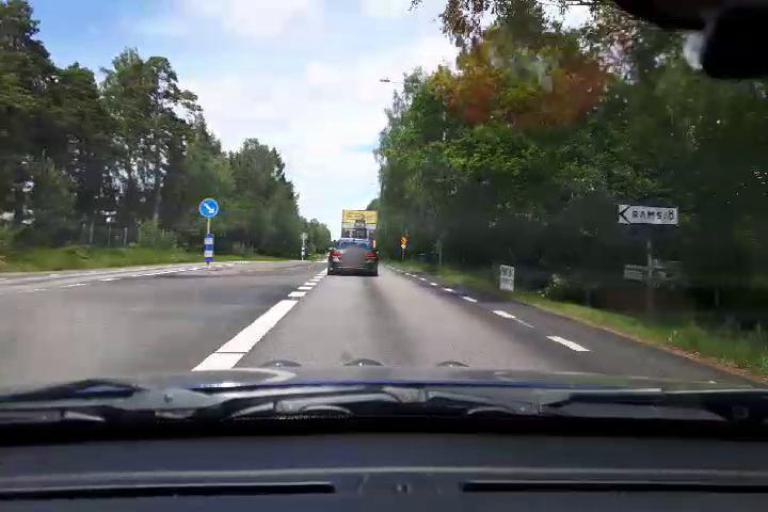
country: SE
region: Uppsala
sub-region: Osthammars Kommun
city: Bjorklinge
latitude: 60.0411
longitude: 17.5508
